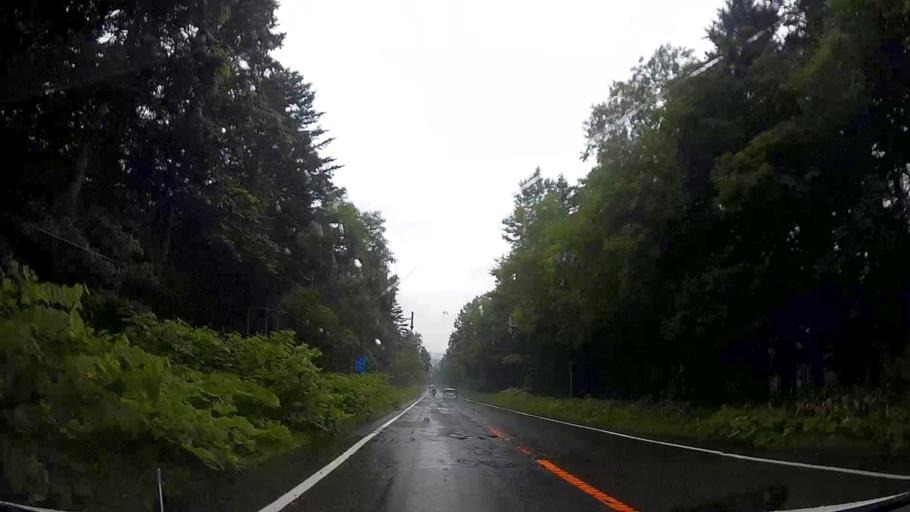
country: JP
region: Hokkaido
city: Shiraoi
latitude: 42.7154
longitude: 141.2398
